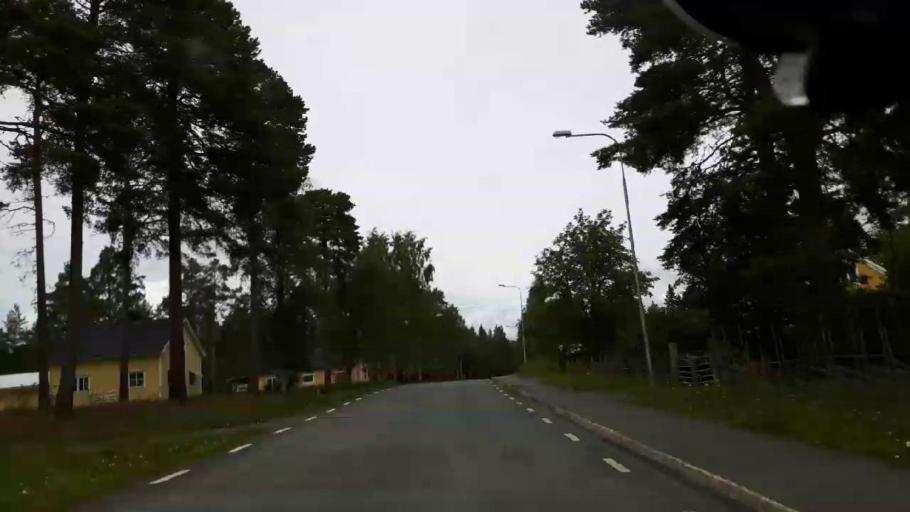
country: SE
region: Jaemtland
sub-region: Krokoms Kommun
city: Valla
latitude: 63.4599
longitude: 14.0621
